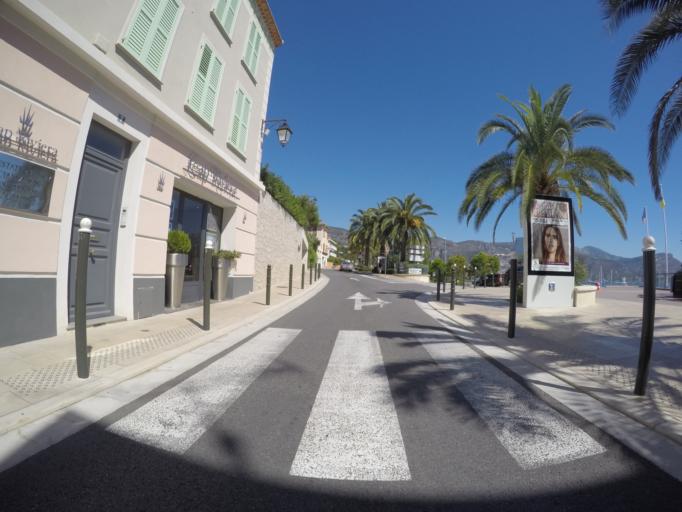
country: FR
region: Provence-Alpes-Cote d'Azur
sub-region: Departement des Alpes-Maritimes
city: Saint-Jean-Cap-Ferrat
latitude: 43.6897
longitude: 7.3333
